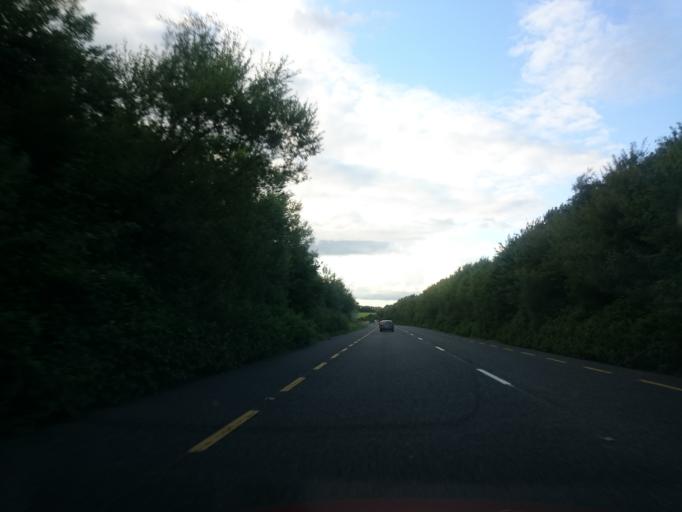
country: IE
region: Leinster
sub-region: Loch Garman
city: Castlebridge
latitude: 52.4083
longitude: -6.5212
